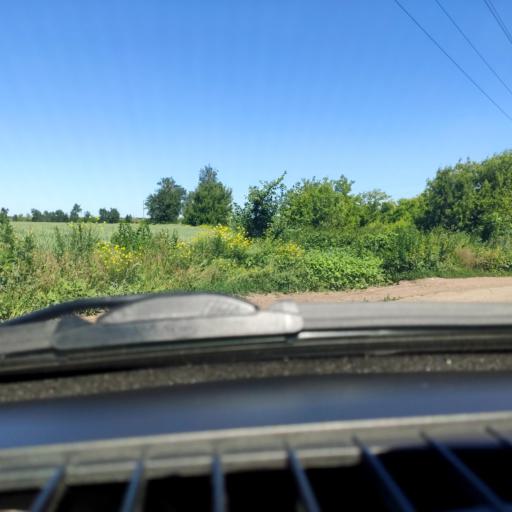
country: RU
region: Samara
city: Tol'yatti
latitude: 53.5920
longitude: 49.4524
